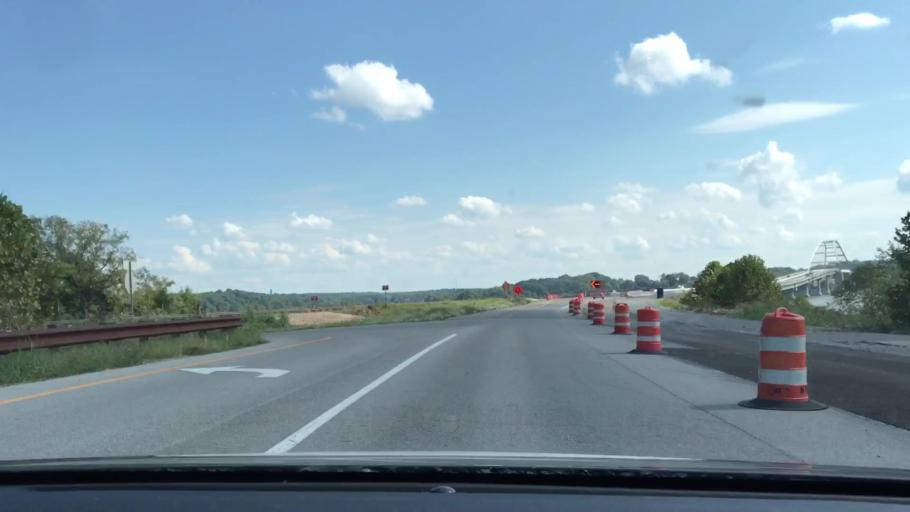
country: US
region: Kentucky
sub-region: Trigg County
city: Cadiz
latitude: 36.8019
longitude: -87.9864
